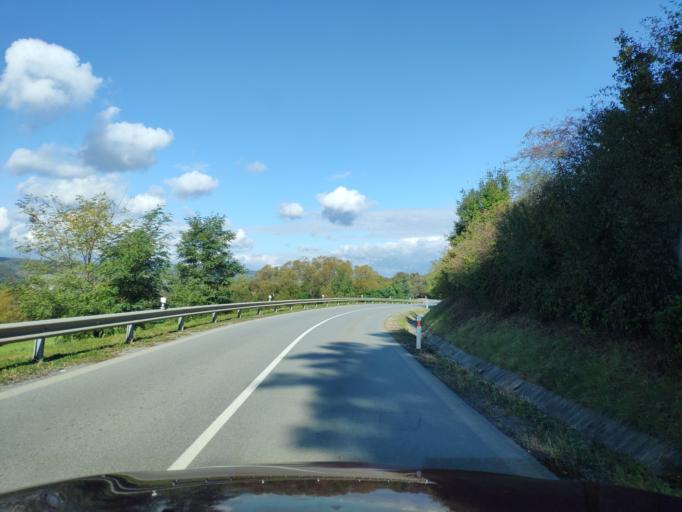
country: SK
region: Presovsky
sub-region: Okres Presov
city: Presov
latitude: 48.8860
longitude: 21.2641
